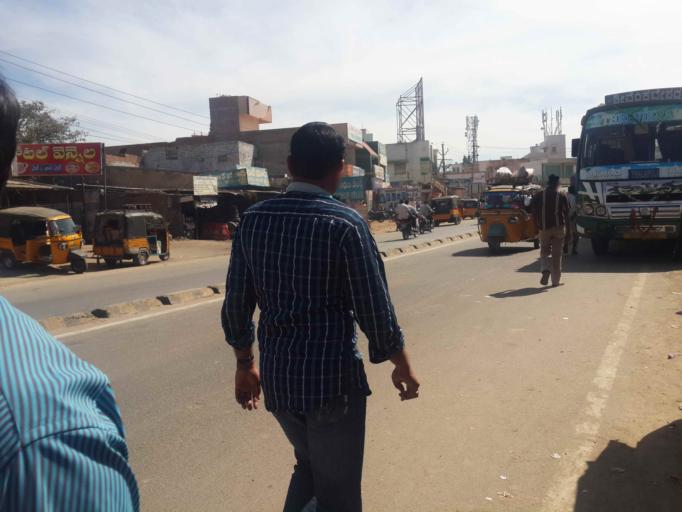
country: IN
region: Andhra Pradesh
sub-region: Anantapur
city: Kadiri
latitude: 14.1154
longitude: 78.1599
